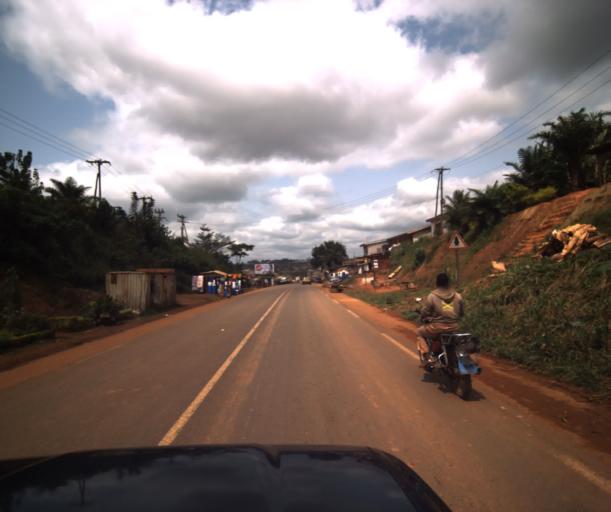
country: CM
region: Centre
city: Yaounde
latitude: 3.7953
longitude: 11.4954
